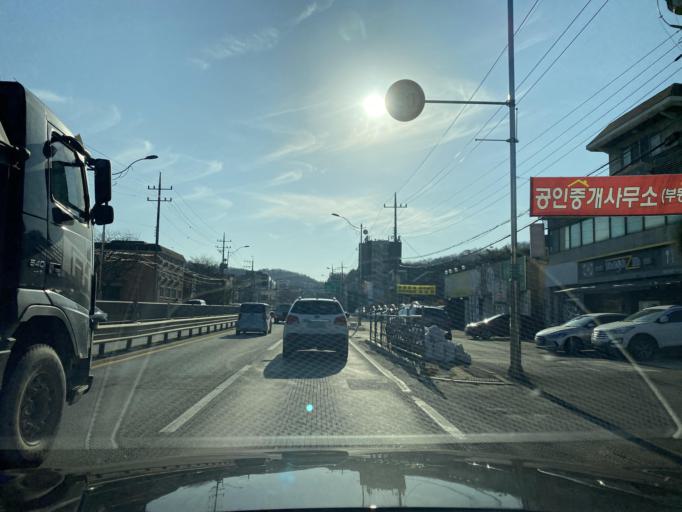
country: KR
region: Chungcheongnam-do
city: Asan
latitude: 36.7761
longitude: 126.9336
